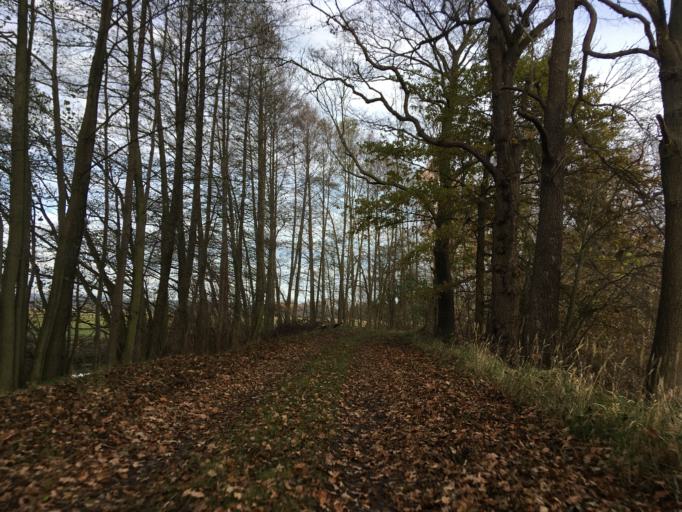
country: DE
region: Brandenburg
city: Schlepzig
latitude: 52.0176
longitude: 13.8580
